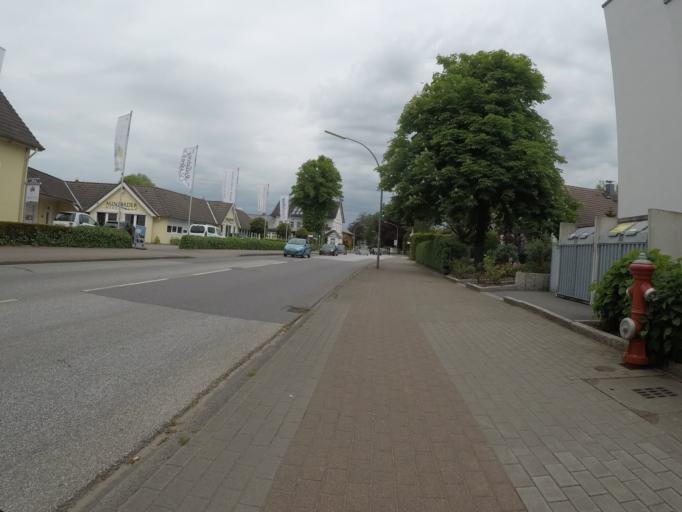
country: DE
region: Schleswig-Holstein
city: Norderstedt
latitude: 53.6745
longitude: 9.9682
